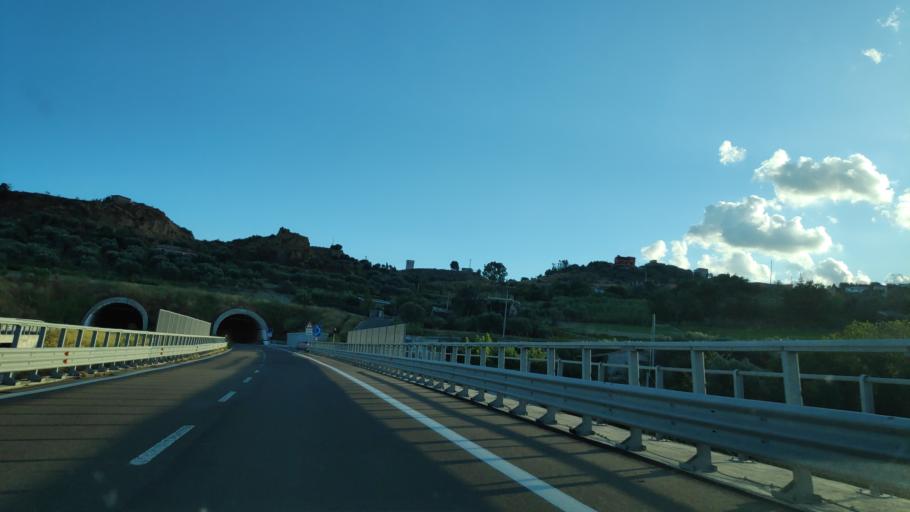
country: IT
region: Calabria
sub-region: Provincia di Reggio Calabria
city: Siderno
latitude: 38.2900
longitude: 16.2801
